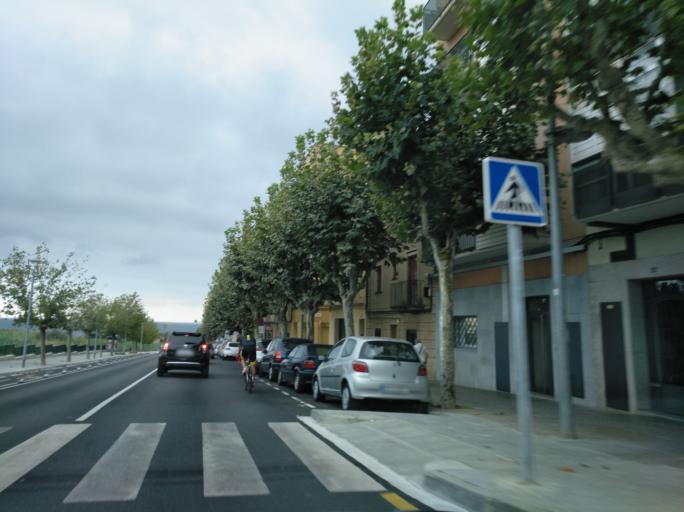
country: ES
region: Catalonia
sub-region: Provincia de Barcelona
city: Mataro
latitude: 41.5448
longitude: 2.4545
